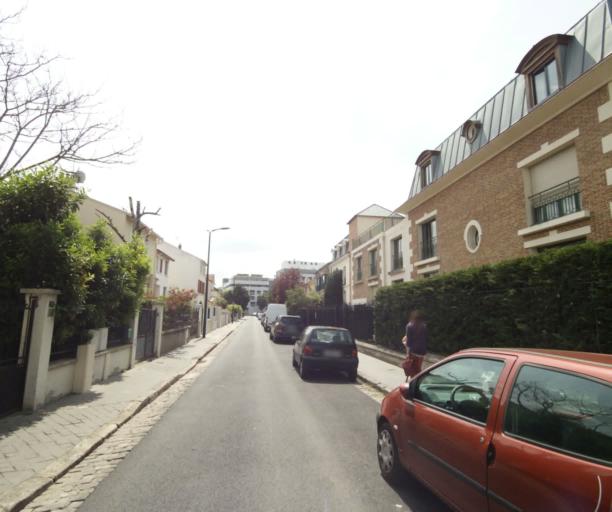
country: FR
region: Ile-de-France
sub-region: Departement des Hauts-de-Seine
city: Colombes
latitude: 48.9280
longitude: 2.2438
